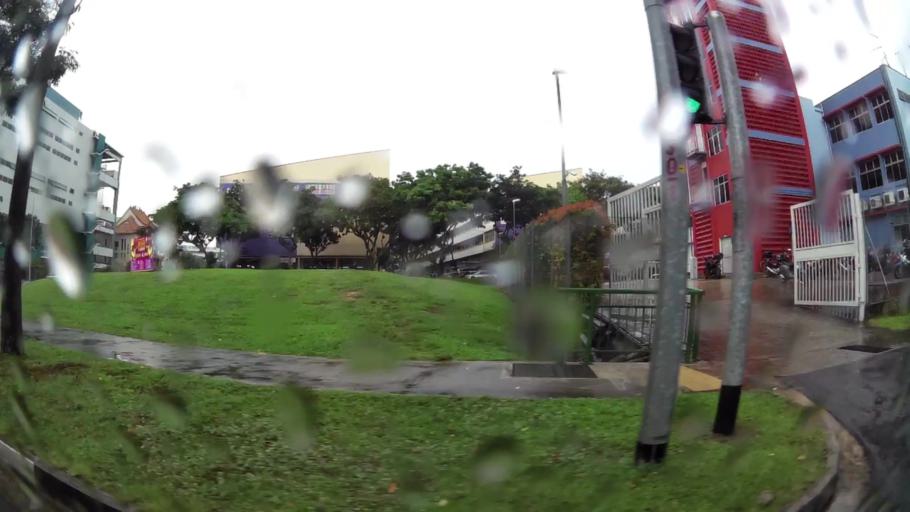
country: SG
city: Singapore
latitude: 1.3346
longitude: 103.9511
